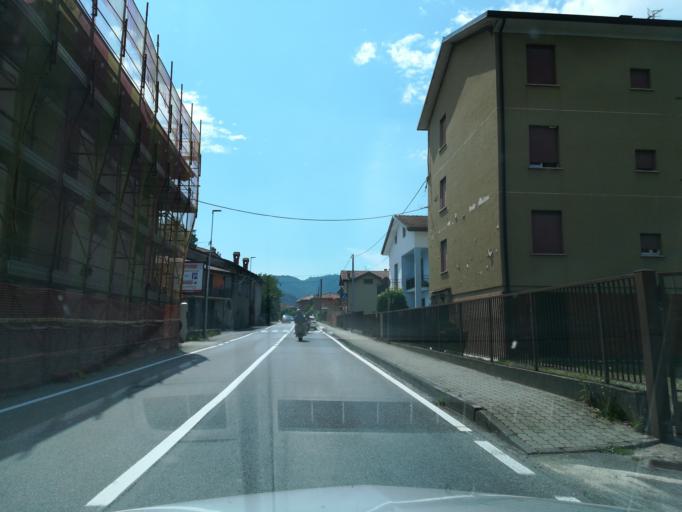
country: IT
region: Lombardy
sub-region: Provincia di Bergamo
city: Ambivere
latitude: 45.7282
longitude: 9.5539
